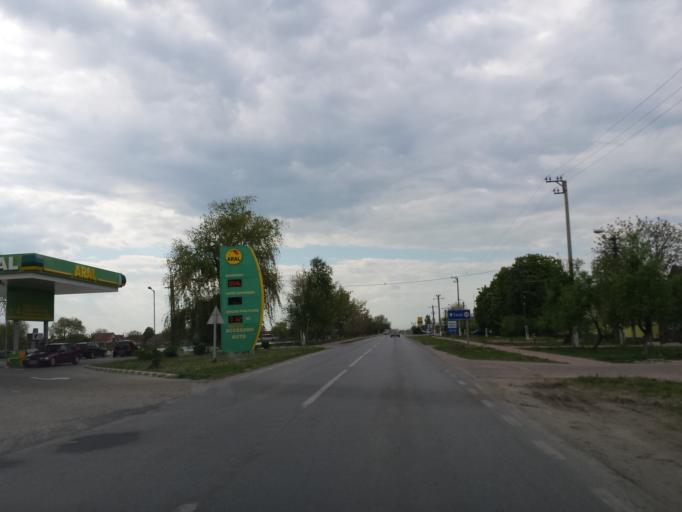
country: RO
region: Timis
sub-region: Oras Sannicolau Mare
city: Sannicolau Mare
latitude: 46.0801
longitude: 20.6222
